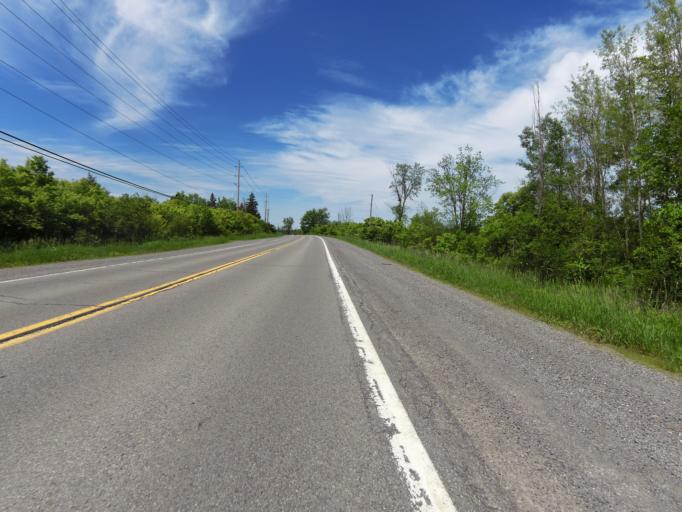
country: CA
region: Ontario
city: Ottawa
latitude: 45.3764
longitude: -75.5764
